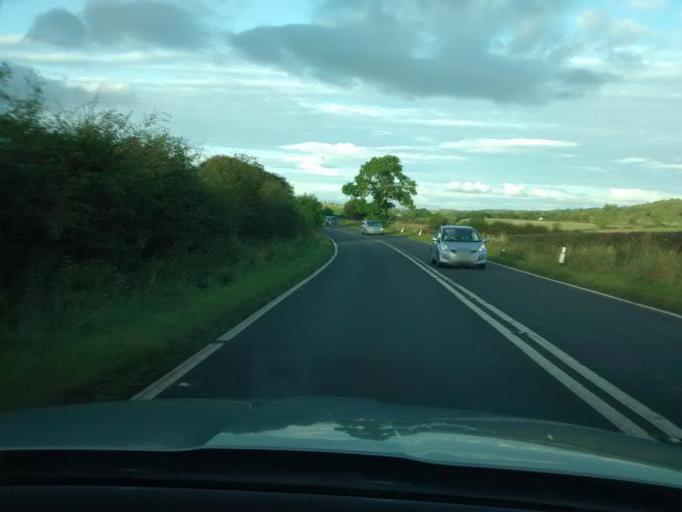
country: GB
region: Scotland
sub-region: Renfrewshire
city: Lochwinnoch
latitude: 55.8000
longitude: -4.5924
